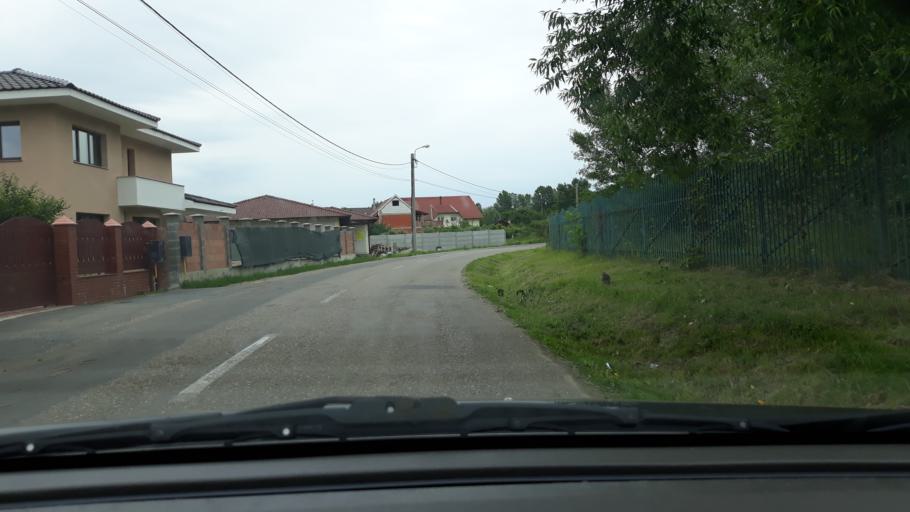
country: RO
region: Bihor
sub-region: Comuna Sanmartin
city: Sanmartin
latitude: 47.0526
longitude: 21.9972
